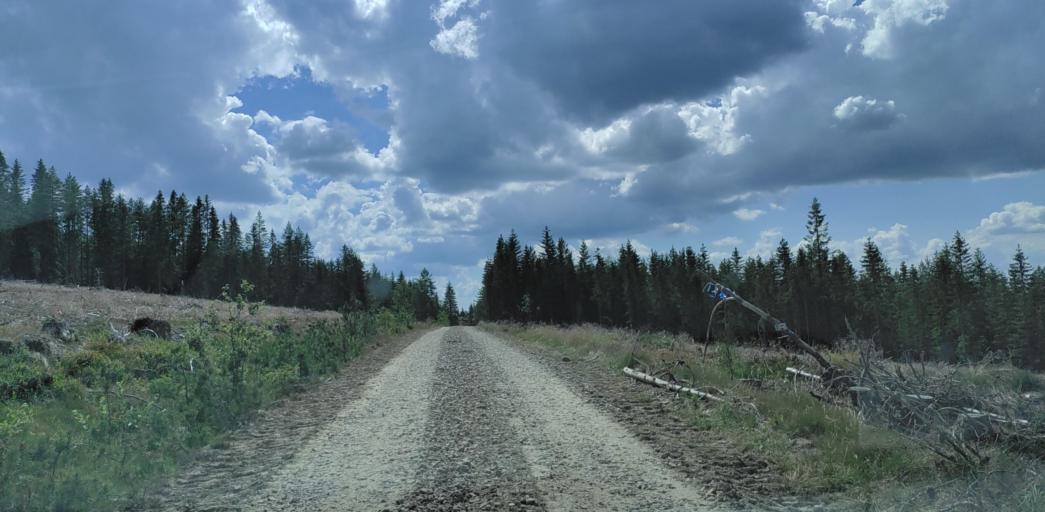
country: SE
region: Vaermland
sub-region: Hagfors Kommun
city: Ekshaerad
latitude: 60.0691
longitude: 13.3437
